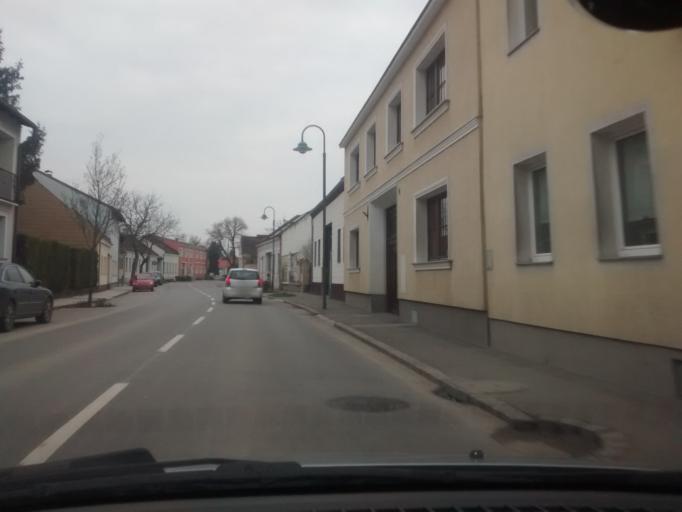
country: AT
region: Lower Austria
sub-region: Politischer Bezirk Wien-Umgebung
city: Gramatneusiedl
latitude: 48.0286
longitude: 16.4886
